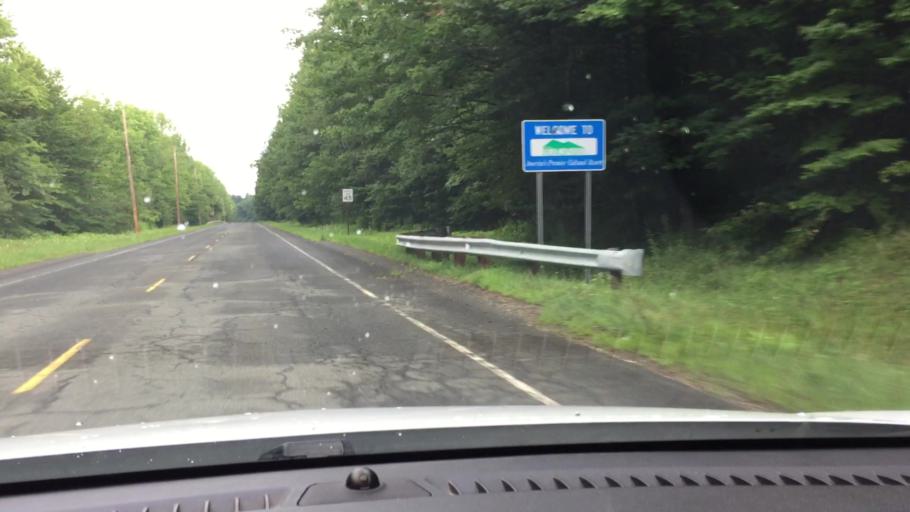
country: US
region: Massachusetts
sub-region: Berkshire County
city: Becket
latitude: 42.4249
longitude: -73.0030
